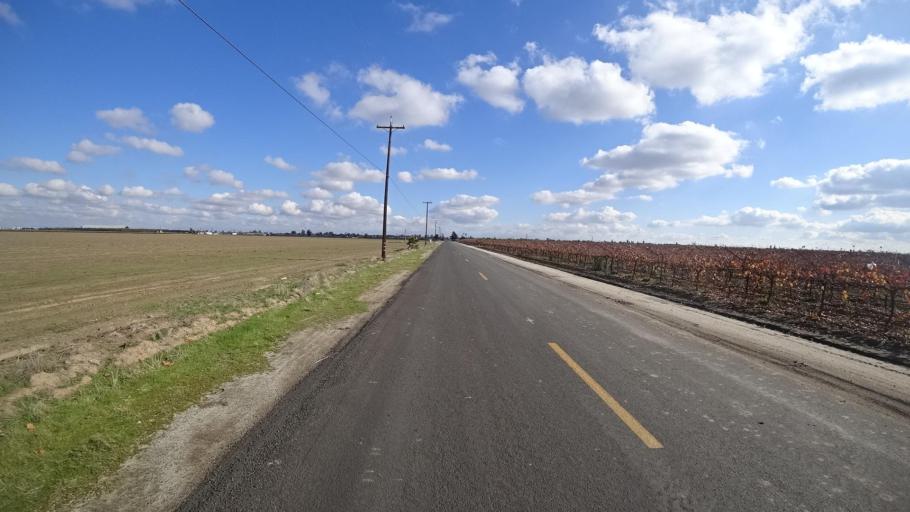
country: US
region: California
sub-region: Kern County
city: McFarland
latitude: 35.6816
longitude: -119.2489
